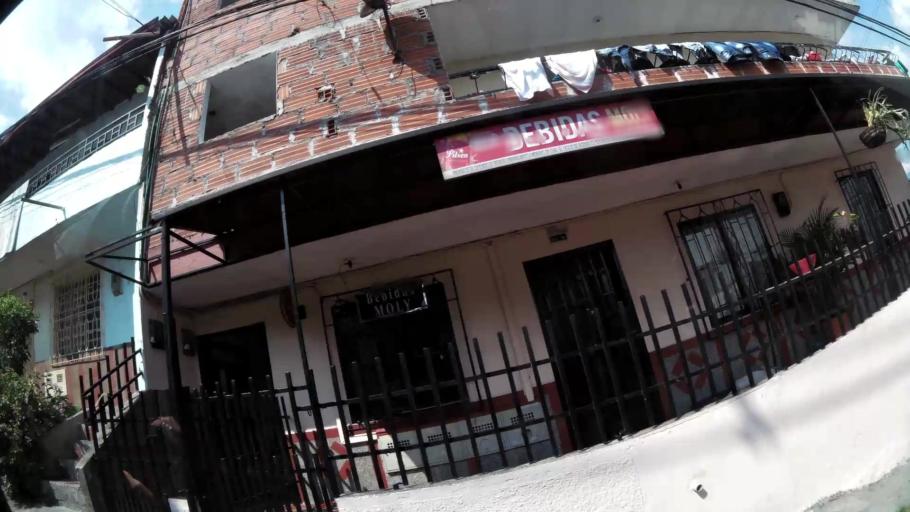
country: CO
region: Antioquia
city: Medellin
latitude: 6.2891
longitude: -75.5927
